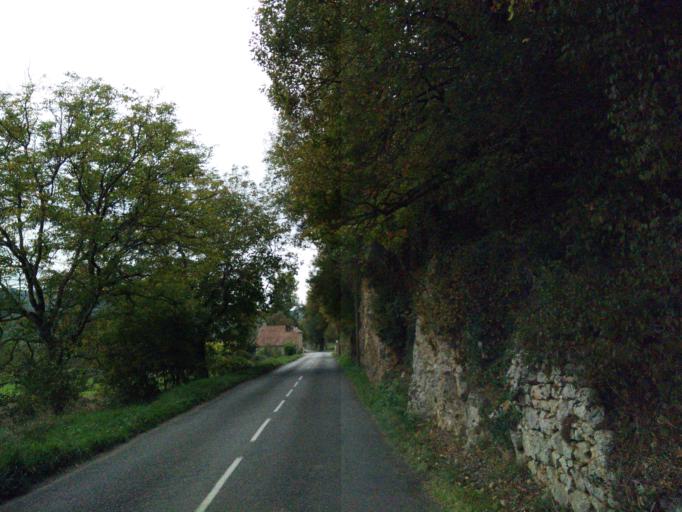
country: FR
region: Midi-Pyrenees
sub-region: Departement du Lot
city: Lalbenque
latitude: 44.4754
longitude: 1.6060
